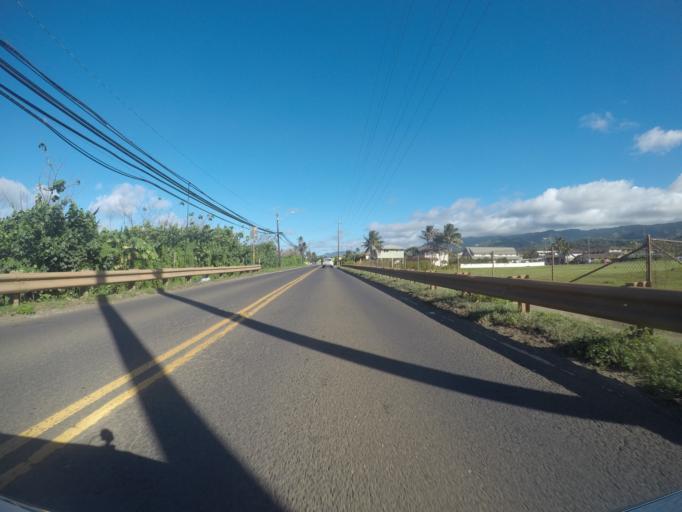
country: US
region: Hawaii
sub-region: Honolulu County
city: La'ie
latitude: 21.6539
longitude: -157.9298
